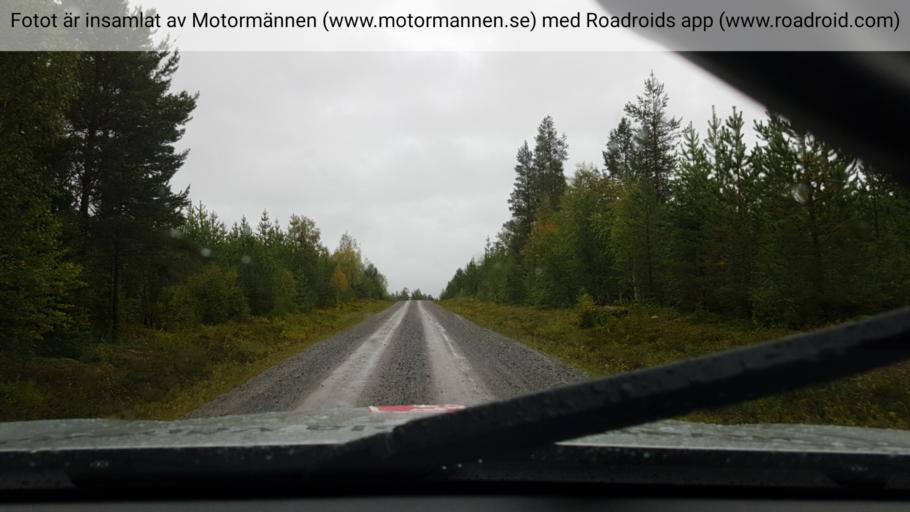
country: SE
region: Vaesterbotten
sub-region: Asele Kommun
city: Asele
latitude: 64.0160
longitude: 17.6362
